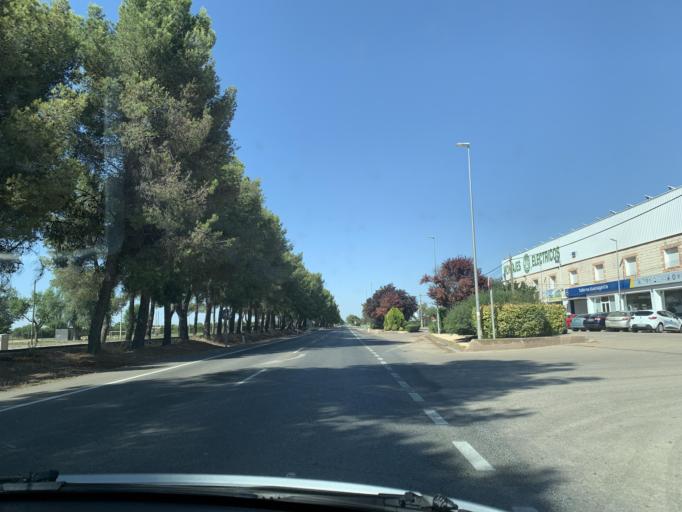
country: ES
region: Castille-La Mancha
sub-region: Provincia de Ciudad Real
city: Argamasilla de Alba
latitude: 39.1315
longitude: -3.0804
